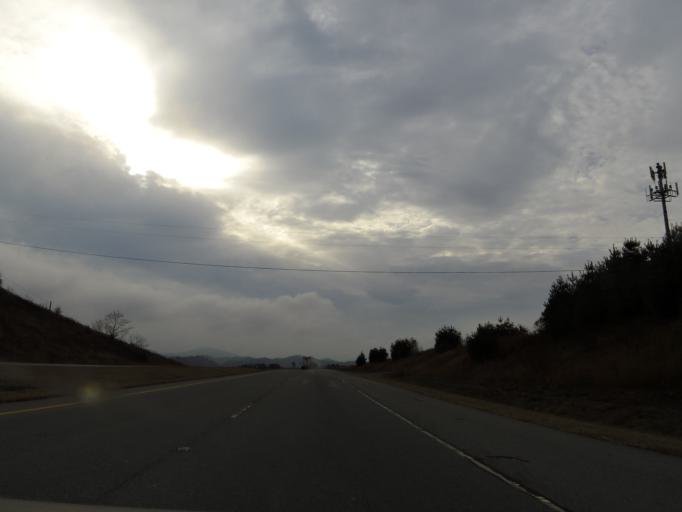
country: US
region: North Carolina
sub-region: Watauga County
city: Boone
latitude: 36.2413
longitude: -81.5489
